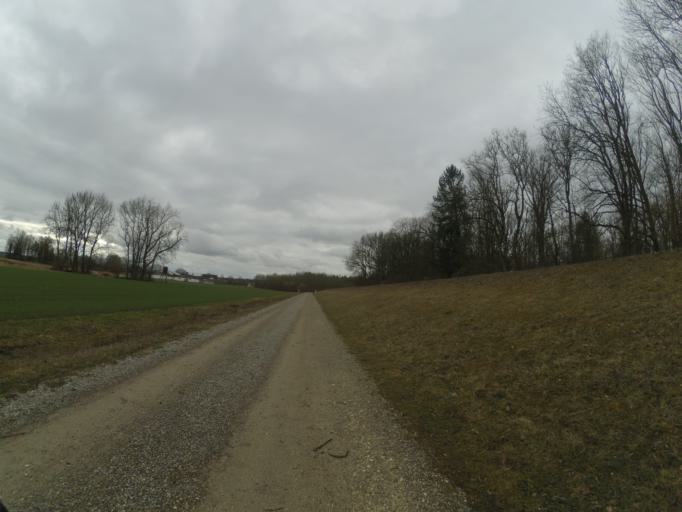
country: DE
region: Bavaria
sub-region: Swabia
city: Senden
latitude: 48.3068
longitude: 10.0468
